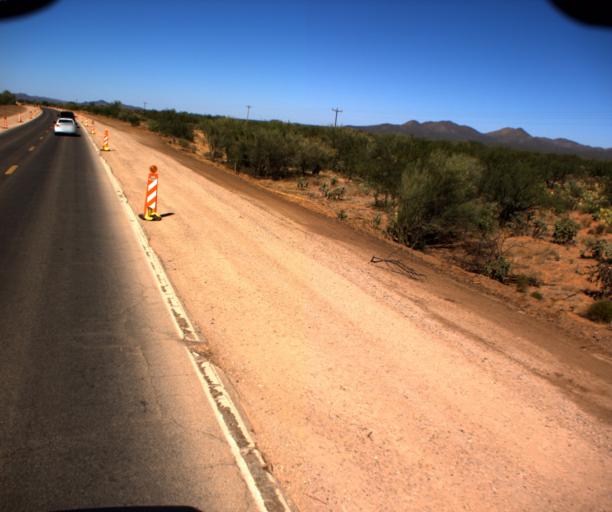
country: US
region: Arizona
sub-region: Pima County
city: Sells
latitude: 31.9776
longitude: -111.7342
